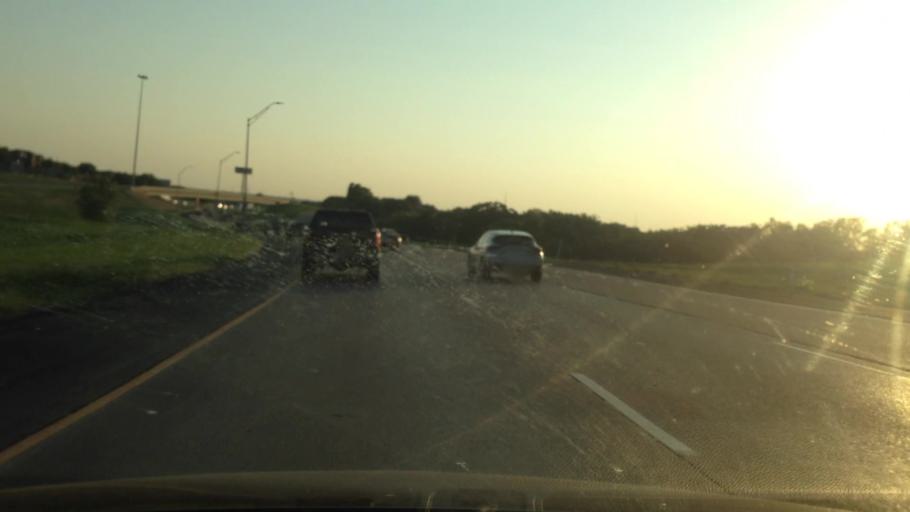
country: US
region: Texas
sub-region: Tarrant County
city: Kennedale
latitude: 32.6716
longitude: -97.2112
